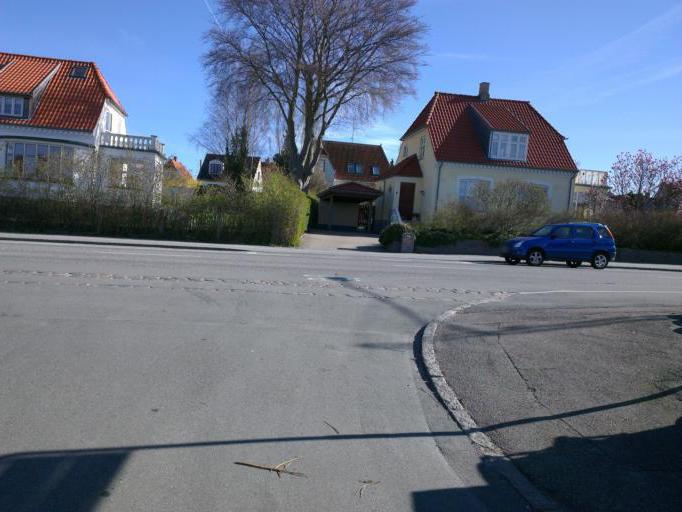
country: DK
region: Capital Region
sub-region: Frederikssund Kommune
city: Frederikssund
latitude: 55.8331
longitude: 12.0708
